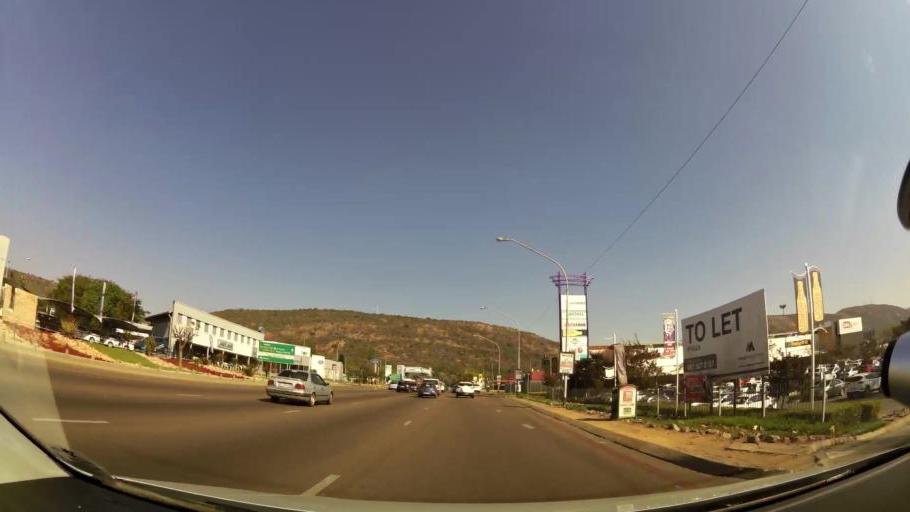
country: ZA
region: Gauteng
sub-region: City of Tshwane Metropolitan Municipality
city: Pretoria
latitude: -25.6823
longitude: 28.1936
